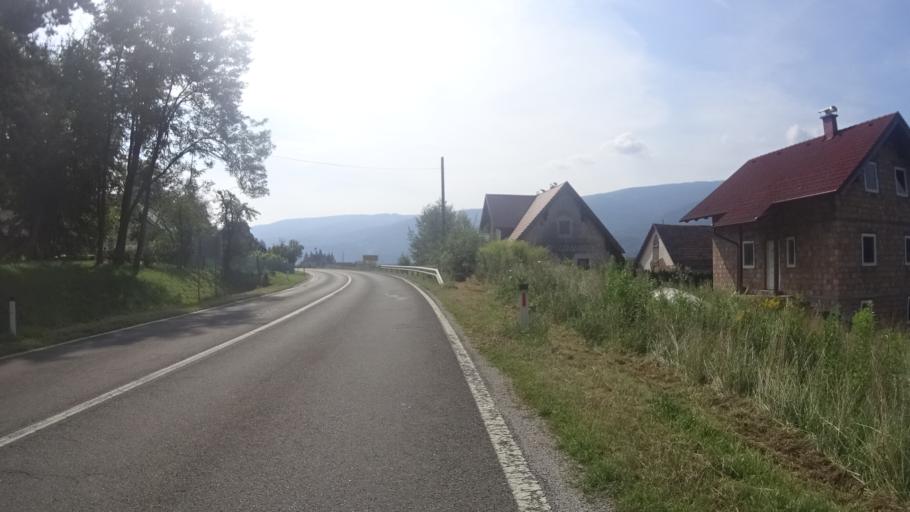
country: SI
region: Selnica ob Dravi
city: Selnica ob Dravi
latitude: 46.5516
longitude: 15.4652
